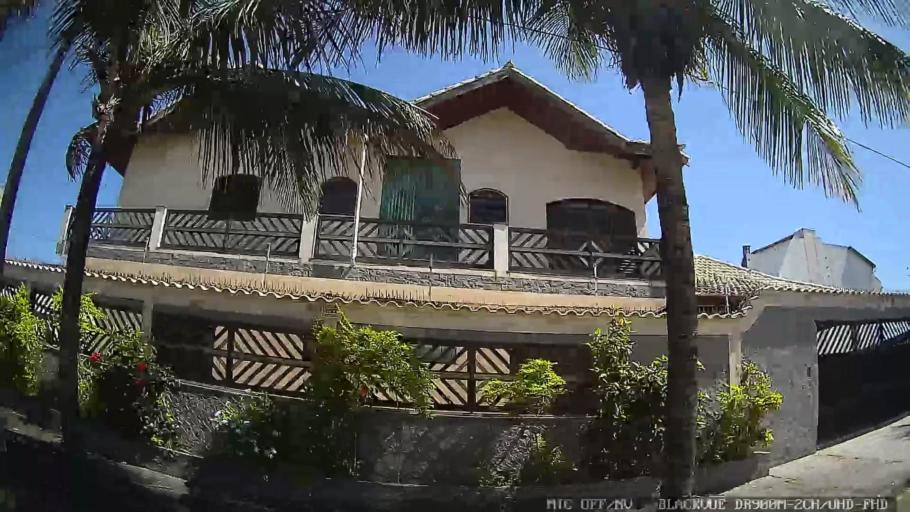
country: BR
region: Sao Paulo
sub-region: Peruibe
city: Peruibe
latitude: -24.3023
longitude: -46.9746
